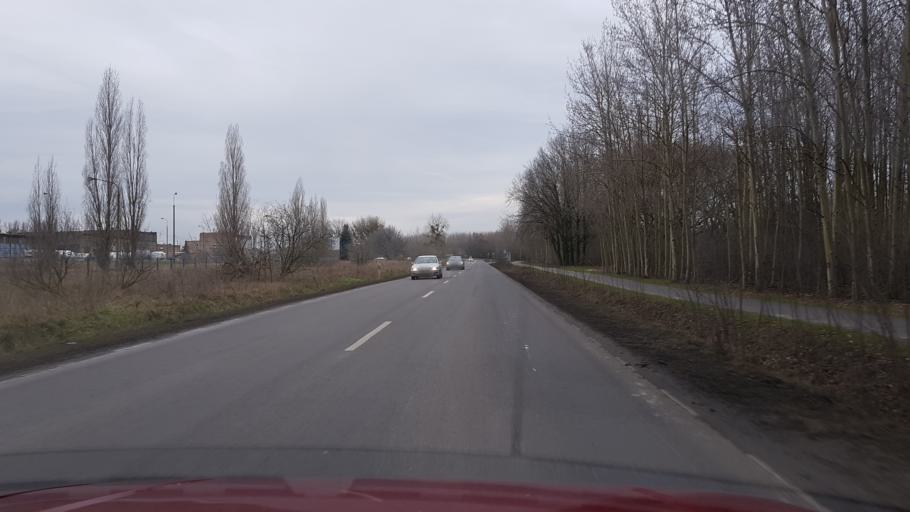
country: PL
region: West Pomeranian Voivodeship
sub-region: Powiat policki
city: Police
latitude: 53.5811
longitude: 14.5531
